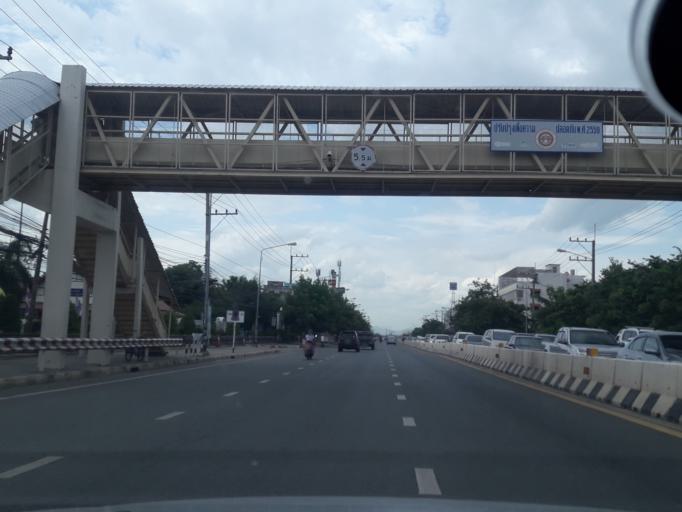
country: TH
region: Sara Buri
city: Saraburi
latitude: 14.5422
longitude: 100.9094
